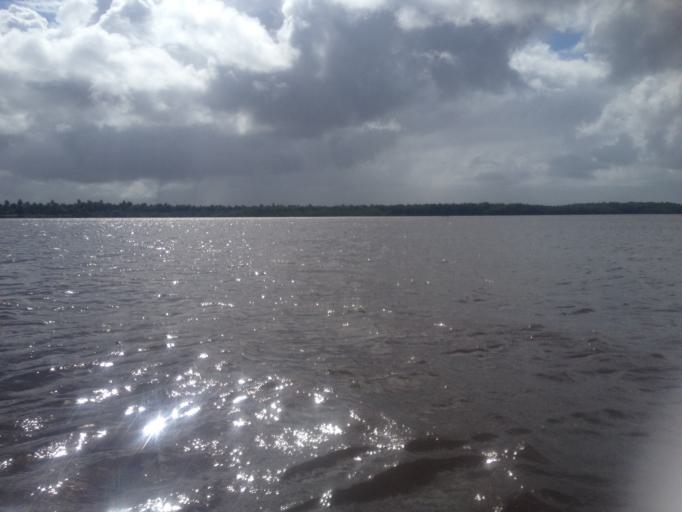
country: BR
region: Sergipe
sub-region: Indiaroba
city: Indiaroba
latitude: -11.4805
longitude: -37.3906
